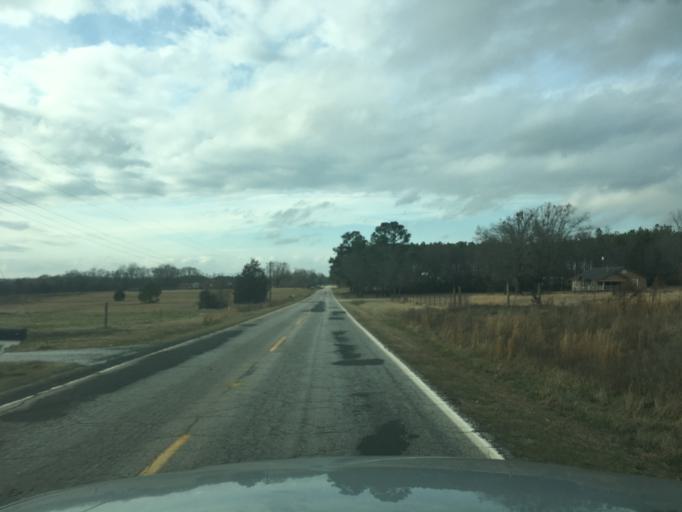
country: US
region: South Carolina
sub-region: Abbeville County
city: Due West
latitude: 34.3312
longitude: -82.4802
